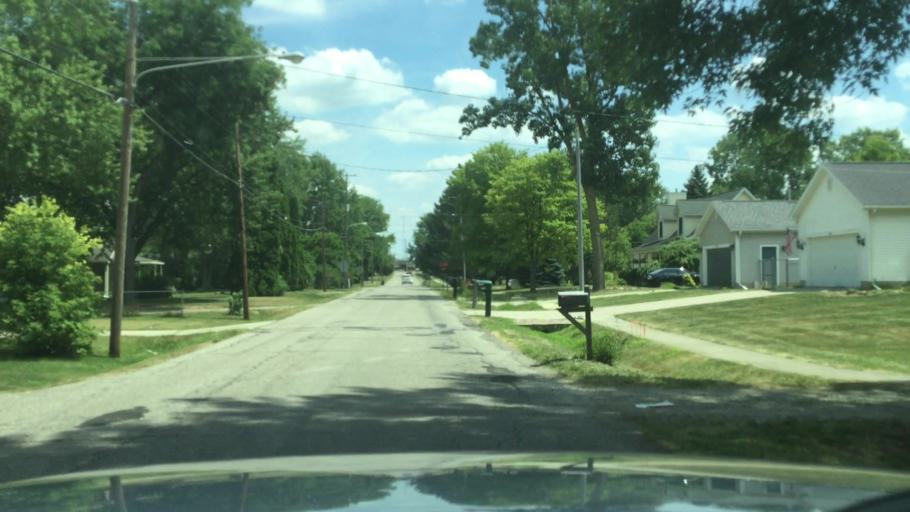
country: US
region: Michigan
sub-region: Genesee County
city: Grand Blanc
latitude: 42.9524
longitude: -83.6643
